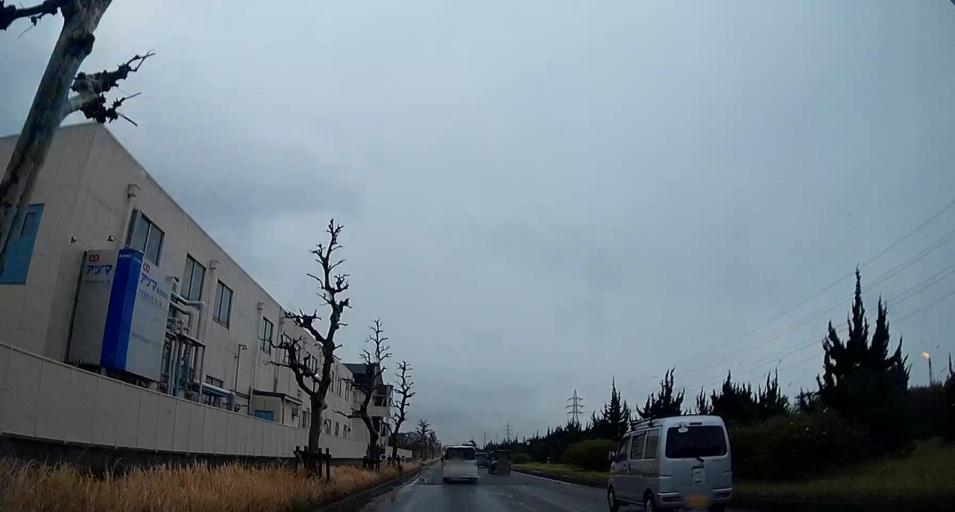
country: JP
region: Chiba
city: Ichihara
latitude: 35.5175
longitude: 140.0601
